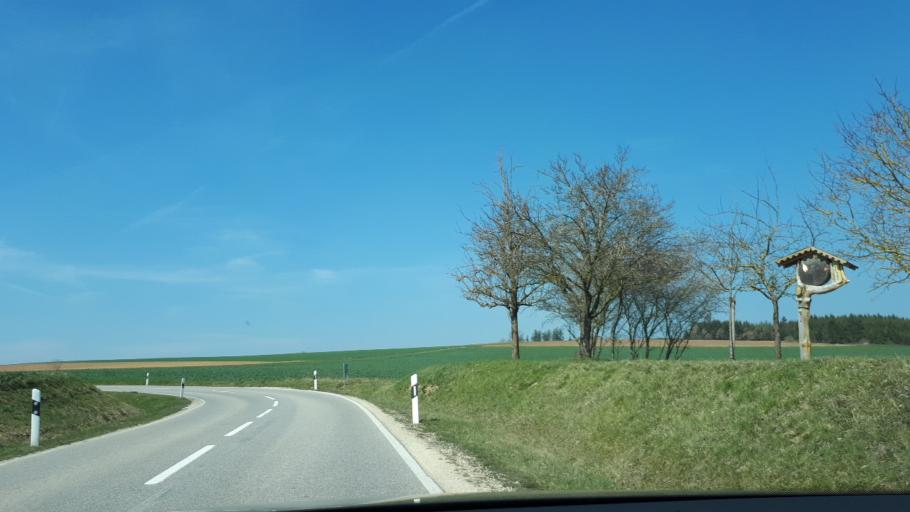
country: DE
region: Bavaria
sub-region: Lower Bavaria
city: Saal
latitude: 48.8810
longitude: 11.9036
